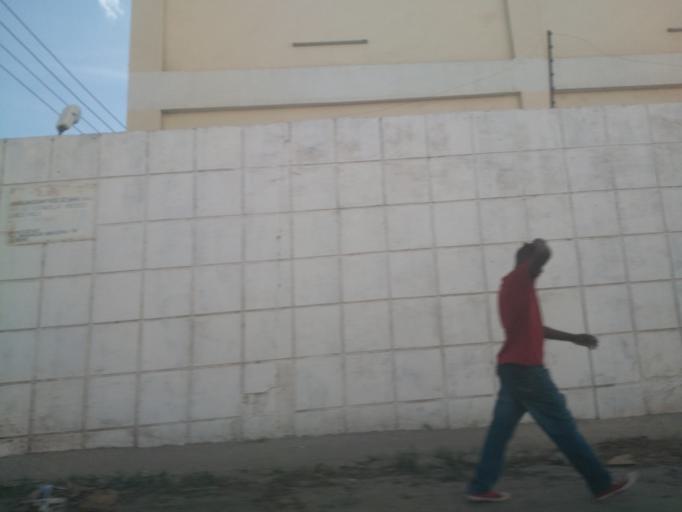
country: TZ
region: Dar es Salaam
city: Dar es Salaam
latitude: -6.8380
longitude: 39.2707
